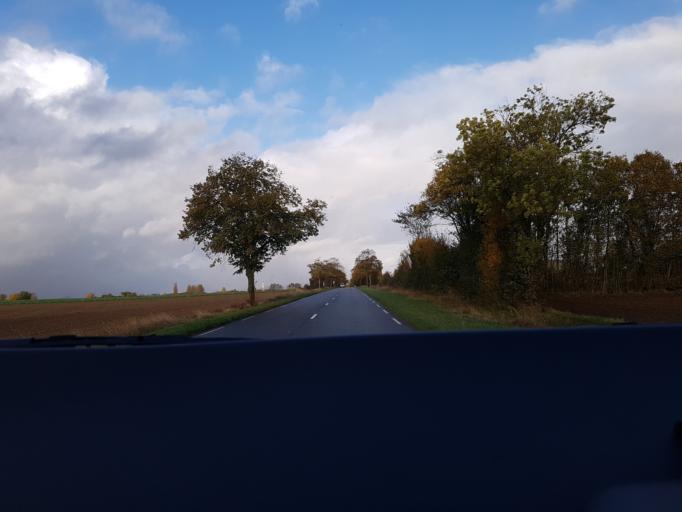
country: FR
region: Poitou-Charentes
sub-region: Departement des Deux-Sevres
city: Brioux-sur-Boutonne
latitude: 46.1164
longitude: -0.2453
